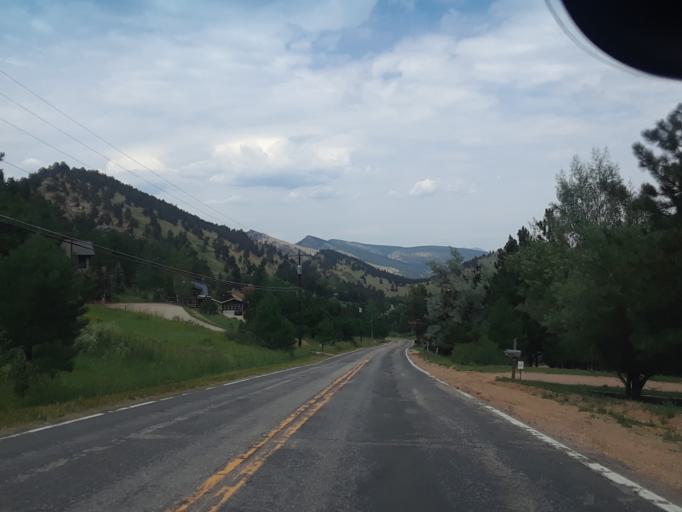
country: US
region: Colorado
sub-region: Boulder County
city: Boulder
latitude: 40.0946
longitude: -105.3019
